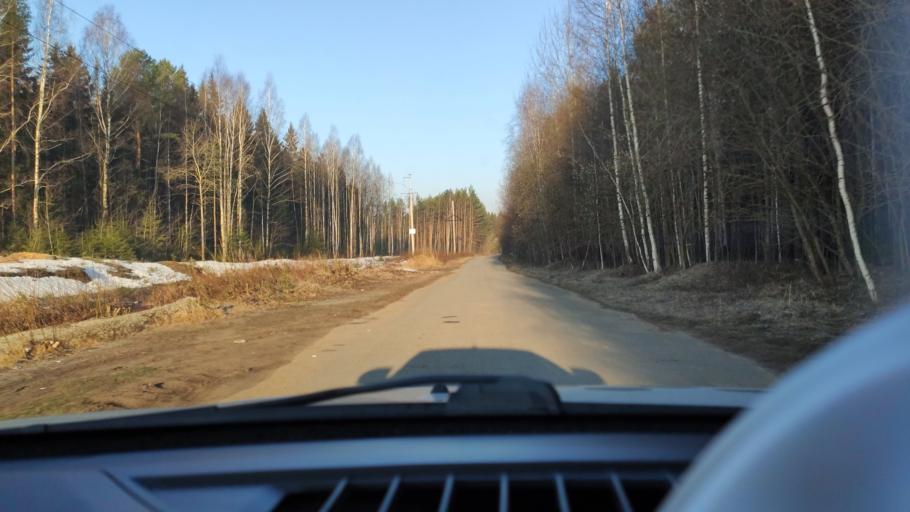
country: RU
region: Perm
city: Polazna
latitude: 58.1451
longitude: 56.4120
